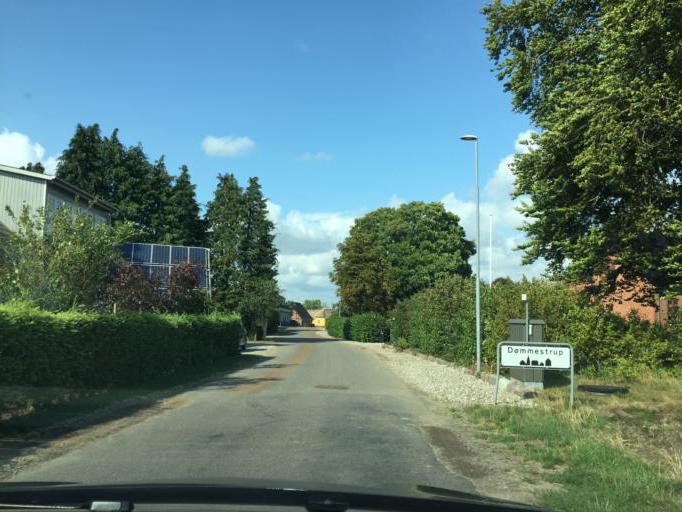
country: DK
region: South Denmark
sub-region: Odense Kommune
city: Bellinge
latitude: 55.3074
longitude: 10.3657
